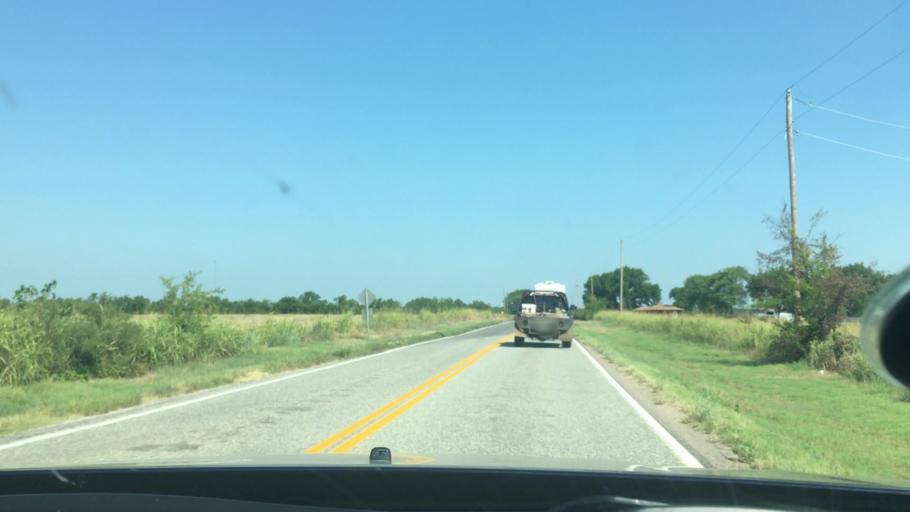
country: US
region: Oklahoma
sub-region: Johnston County
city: Tishomingo
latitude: 34.1834
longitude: -96.5137
